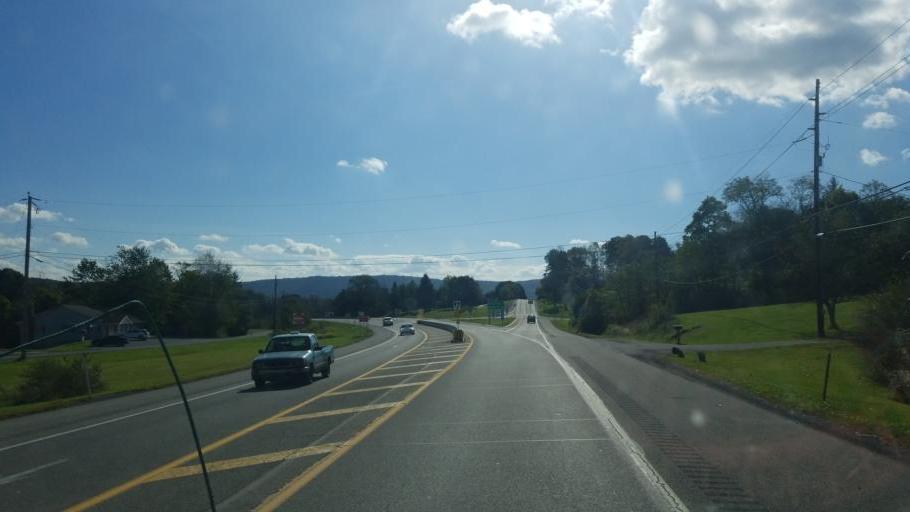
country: US
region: Pennsylvania
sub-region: Bedford County
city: Bedford
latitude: 40.0380
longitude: -78.5243
